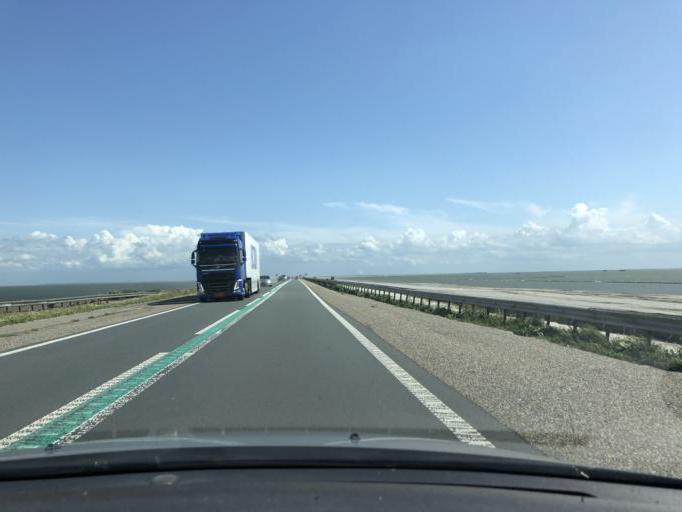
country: NL
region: North Holland
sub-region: Gemeente Enkhuizen
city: Enkhuizen
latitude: 52.6852
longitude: 5.3249
